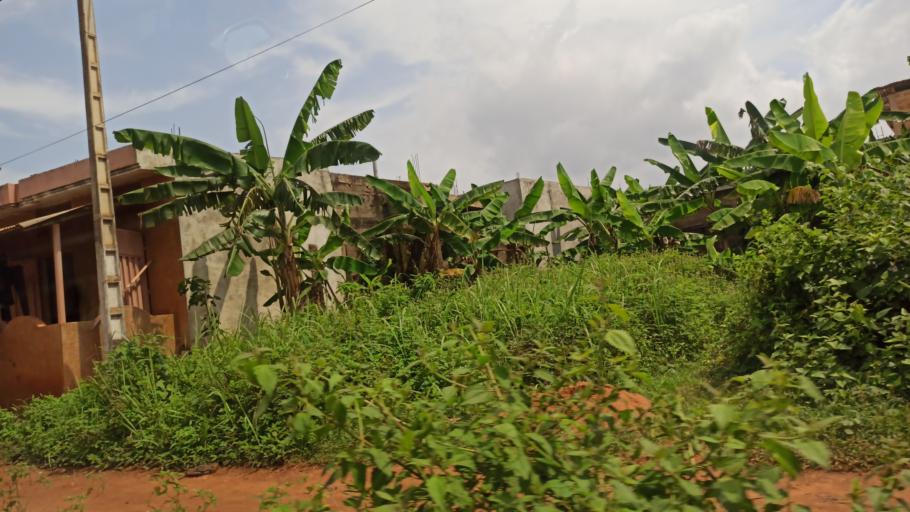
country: BJ
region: Queme
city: Porto-Novo
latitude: 6.4843
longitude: 2.5911
